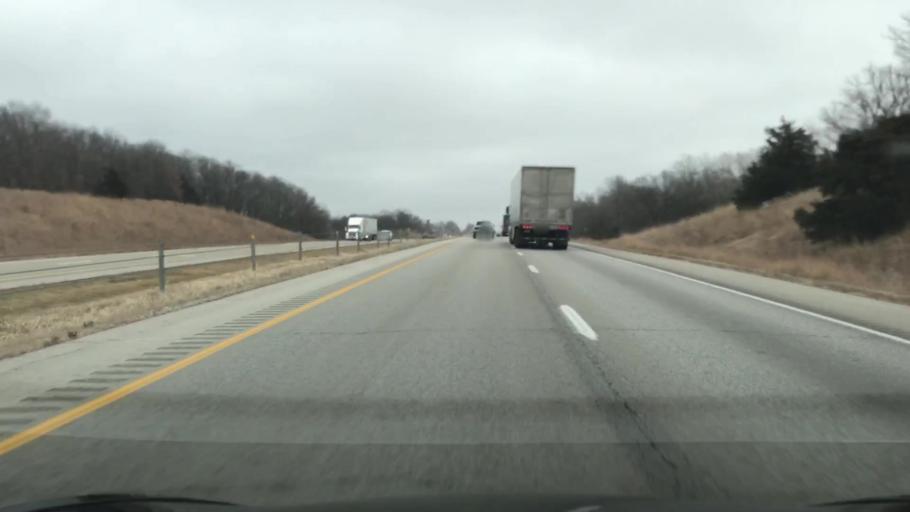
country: US
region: Iowa
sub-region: Madison County
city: Earlham
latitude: 41.5178
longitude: -94.1366
